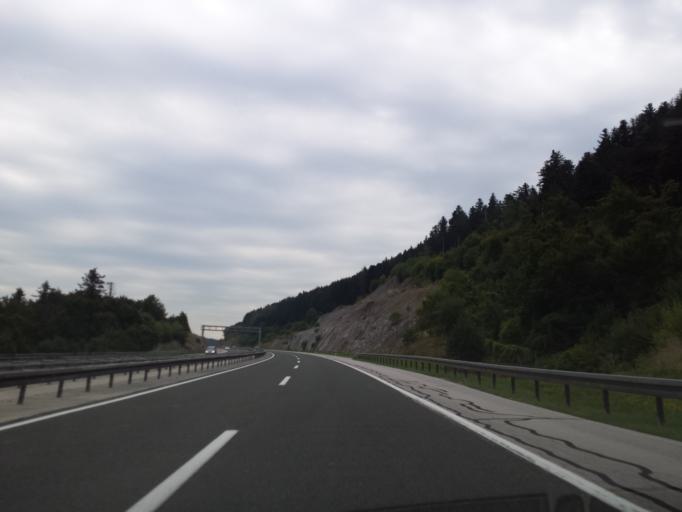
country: HR
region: Licko-Senjska
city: Otocac
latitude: 44.8605
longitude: 15.2126
